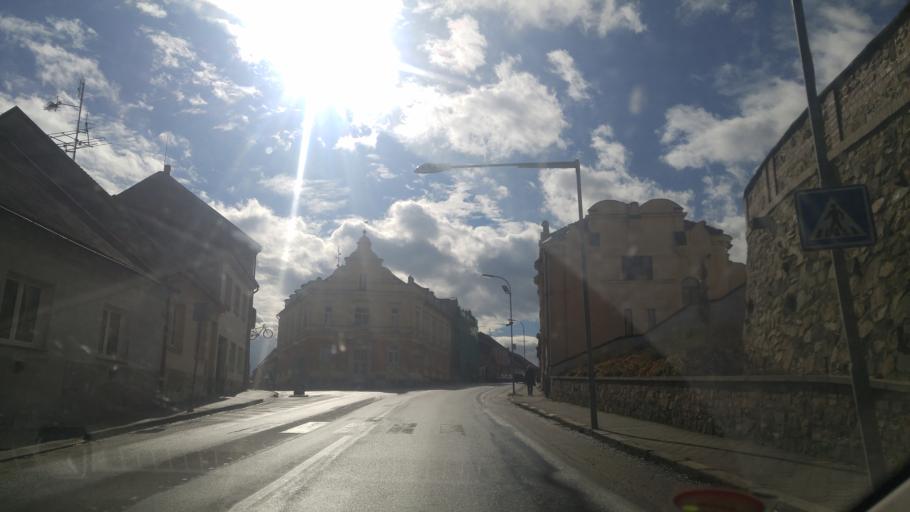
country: CZ
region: Jihocesky
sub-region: Okres Tabor
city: Veseli nad Luznici
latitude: 49.1842
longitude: 14.6976
